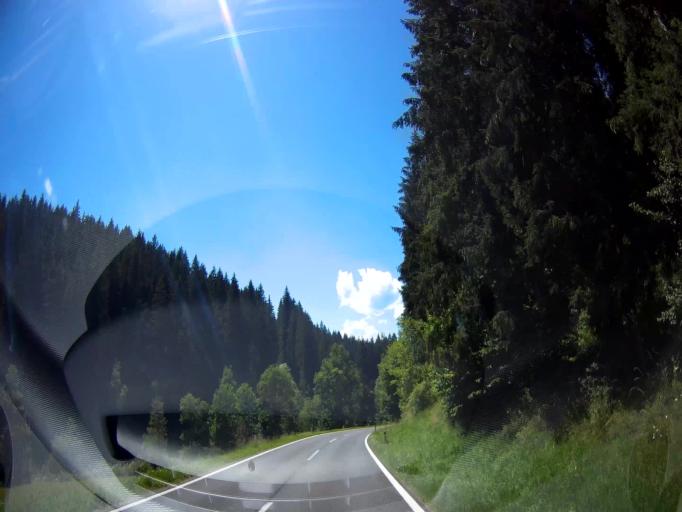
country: AT
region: Carinthia
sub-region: Politischer Bezirk Sankt Veit an der Glan
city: Glodnitz
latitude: 46.8507
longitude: 14.1463
